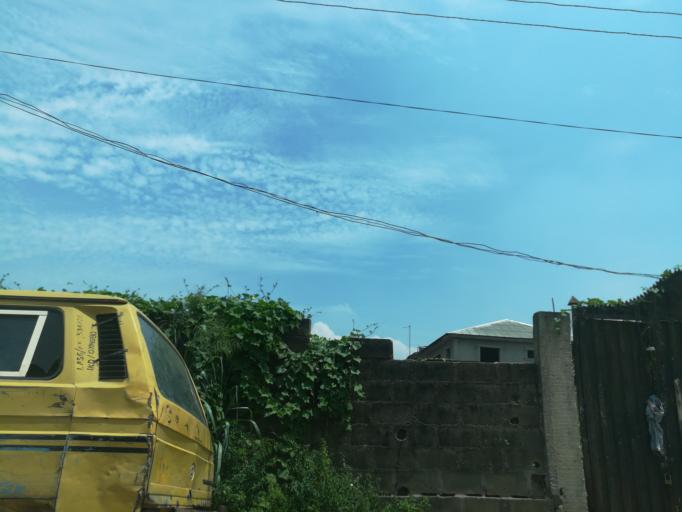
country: NG
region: Lagos
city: Ikorodu
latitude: 6.6225
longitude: 3.4926
